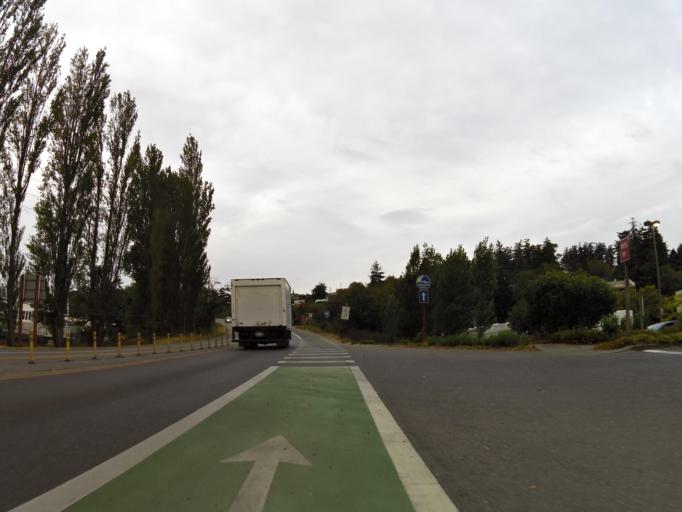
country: US
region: Washington
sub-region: Jefferson County
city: Port Townsend
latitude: 48.1075
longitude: -122.7819
